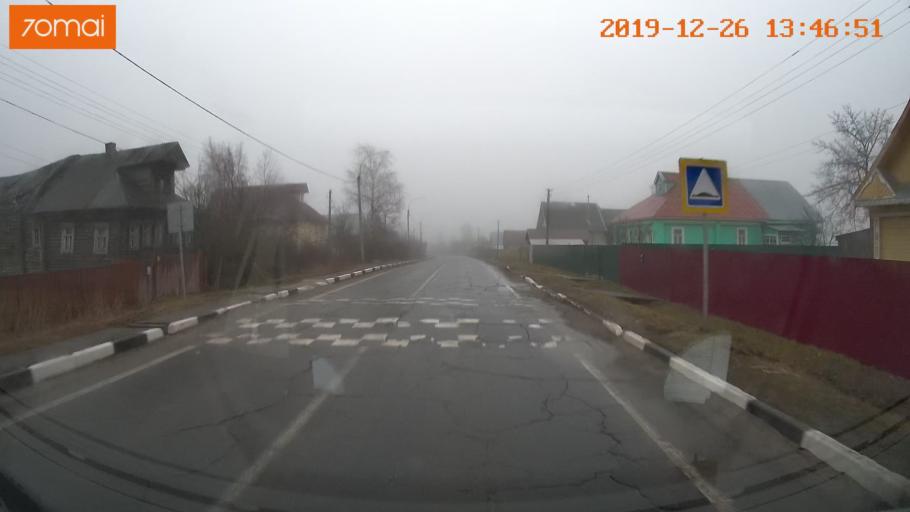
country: RU
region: Vologda
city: Sheksna
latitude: 58.6886
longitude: 38.5296
